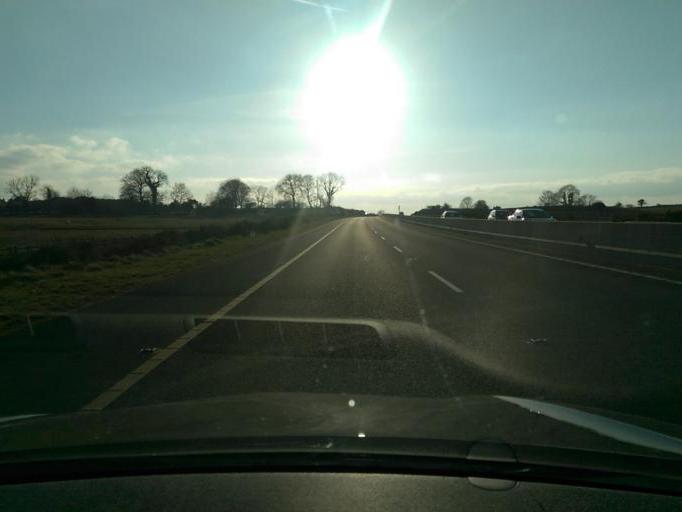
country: IE
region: Munster
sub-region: North Tipperary
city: Roscrea
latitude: 52.9110
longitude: -7.8415
